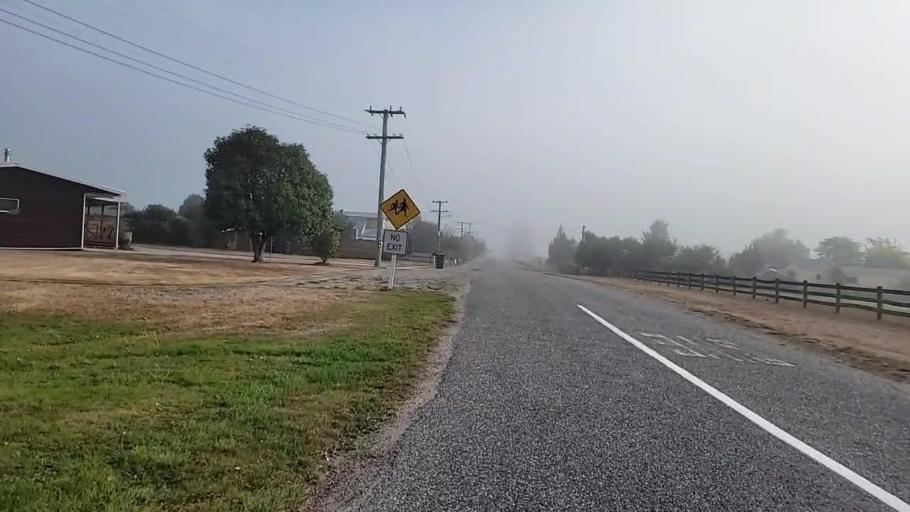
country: NZ
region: Southland
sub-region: Gore District
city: Gore
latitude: -45.6325
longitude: 169.3617
